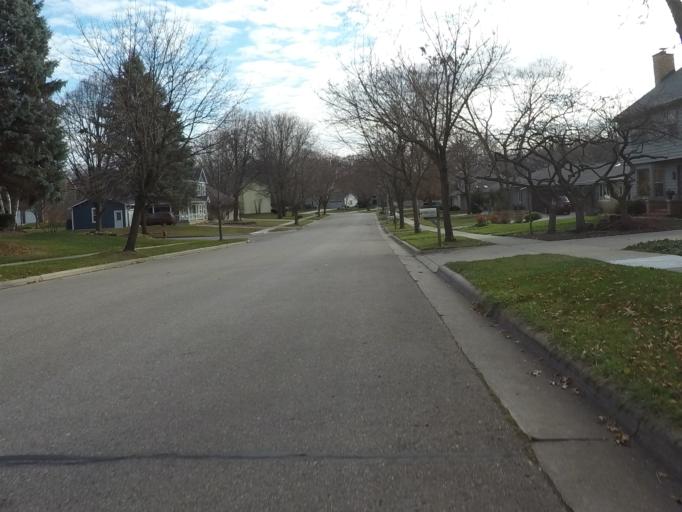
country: US
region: Wisconsin
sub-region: Dane County
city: Middleton
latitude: 43.0739
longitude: -89.5164
